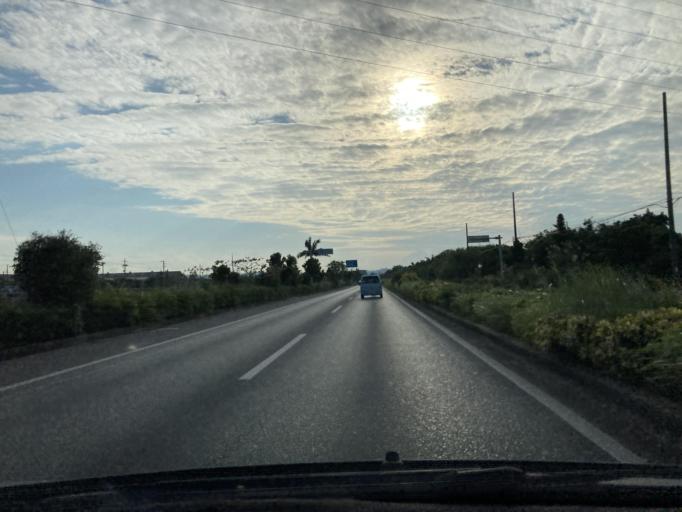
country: JP
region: Okinawa
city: Katsuren-haebaru
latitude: 26.3351
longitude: 127.8429
